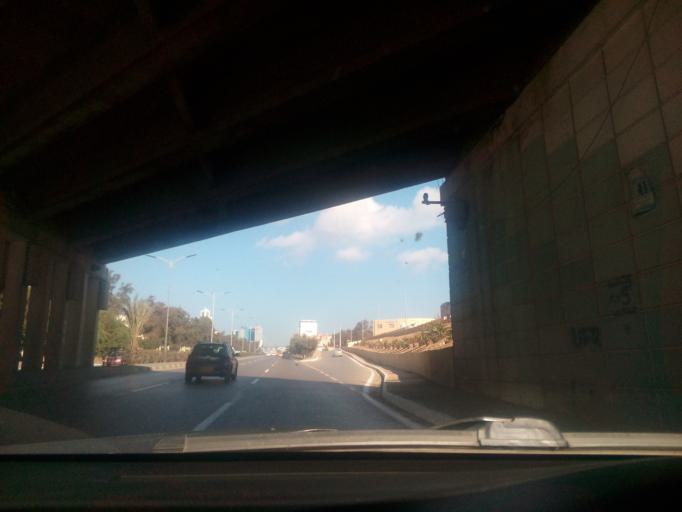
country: DZ
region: Oran
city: Oran
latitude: 35.6887
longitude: -0.6076
